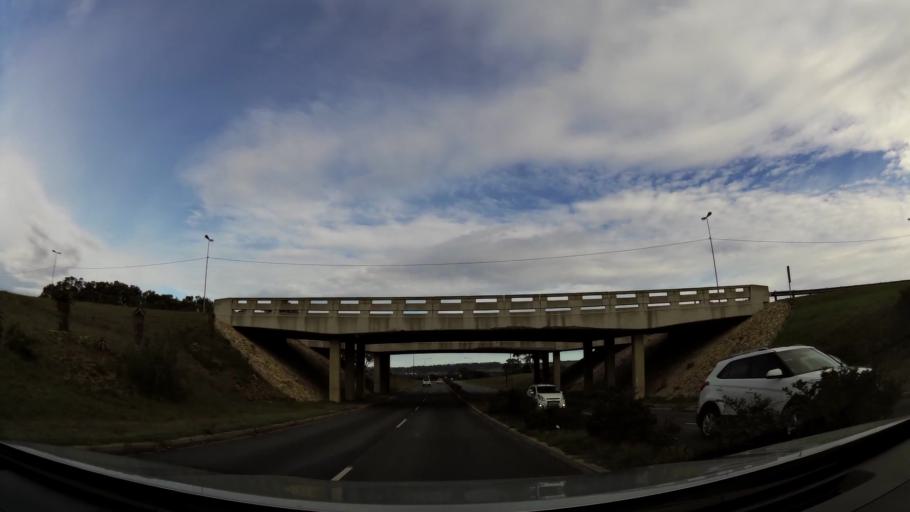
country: ZA
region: Eastern Cape
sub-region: Nelson Mandela Bay Metropolitan Municipality
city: Port Elizabeth
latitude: -33.9482
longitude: 25.5111
